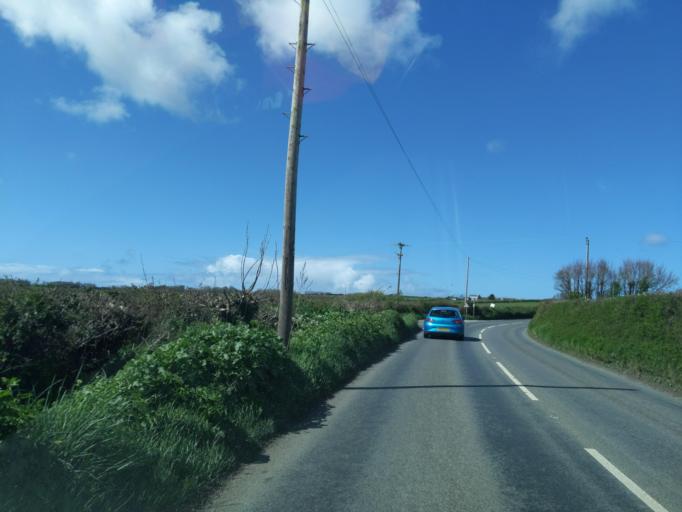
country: GB
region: England
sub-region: Cornwall
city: Wadebridge
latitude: 50.5428
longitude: -4.8626
